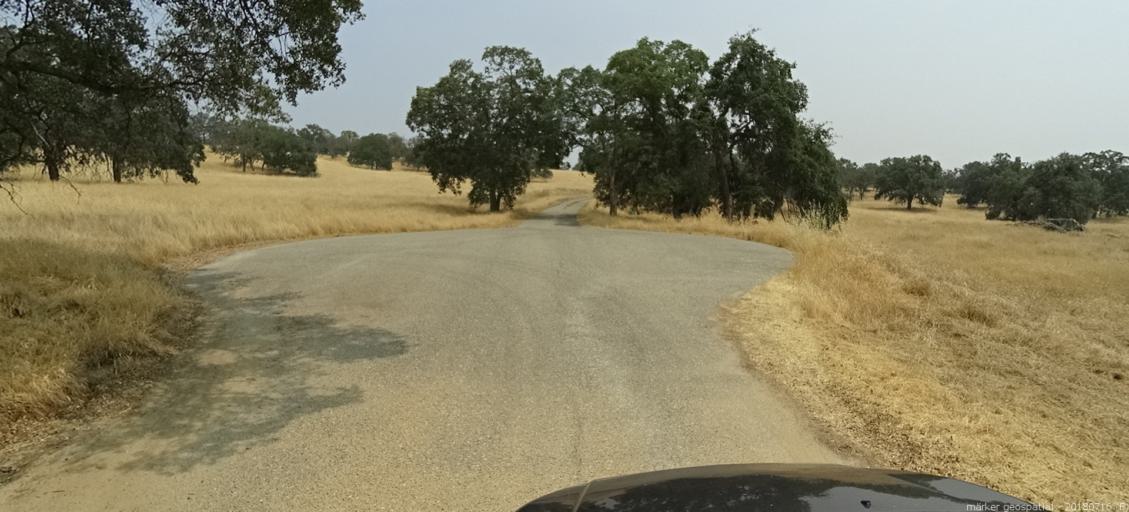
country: US
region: California
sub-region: Madera County
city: Yosemite Lakes
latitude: 37.2384
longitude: -119.7979
